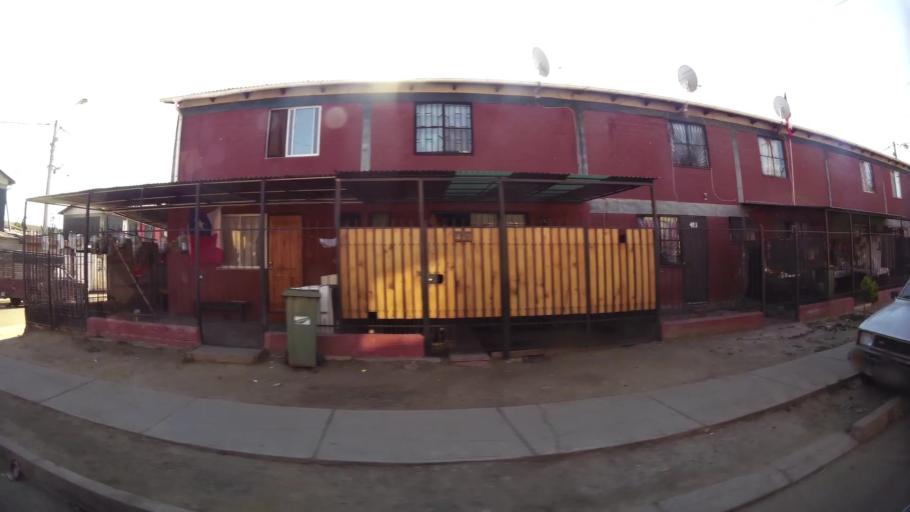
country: CL
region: Santiago Metropolitan
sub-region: Provincia de Talagante
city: Penaflor
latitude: -33.6030
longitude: -70.8649
